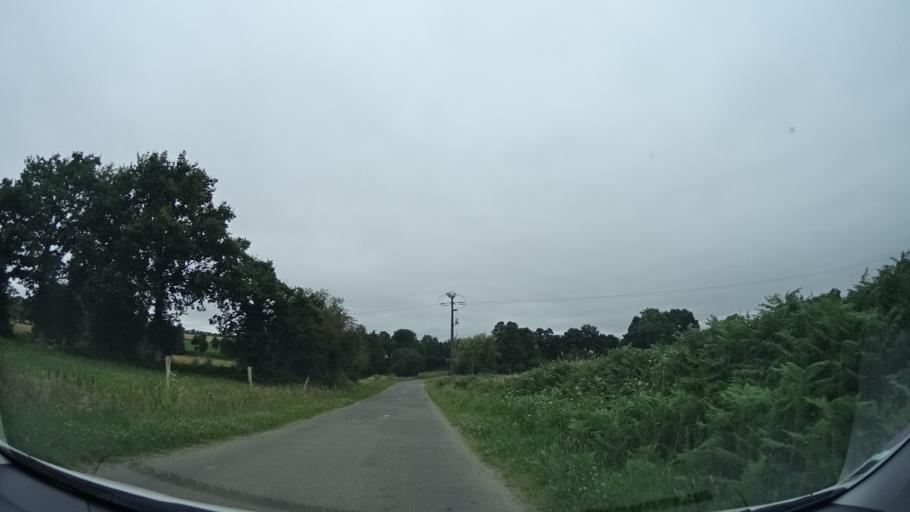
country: FR
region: Brittany
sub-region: Departement d'Ille-et-Vilaine
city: Irodouer
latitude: 48.3173
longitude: -1.9324
